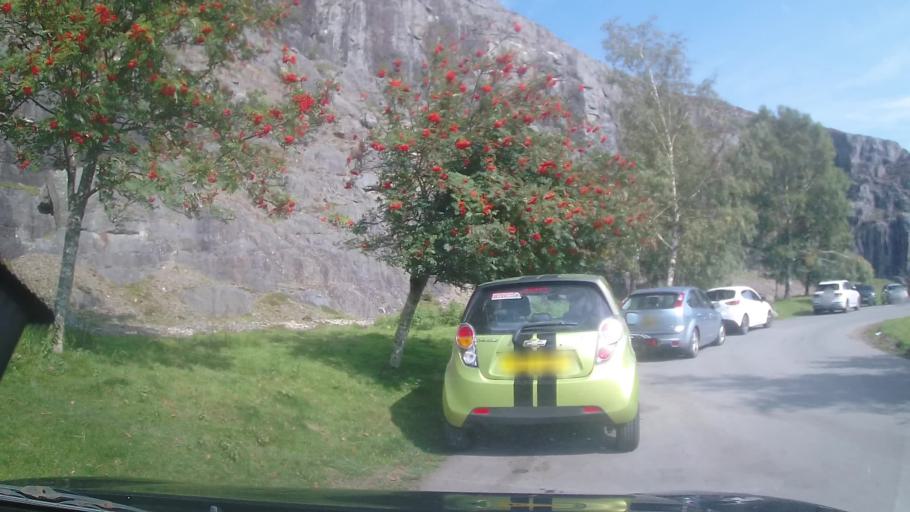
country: GB
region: Wales
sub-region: Sir Powys
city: Rhayader
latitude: 52.2695
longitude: -3.5783
